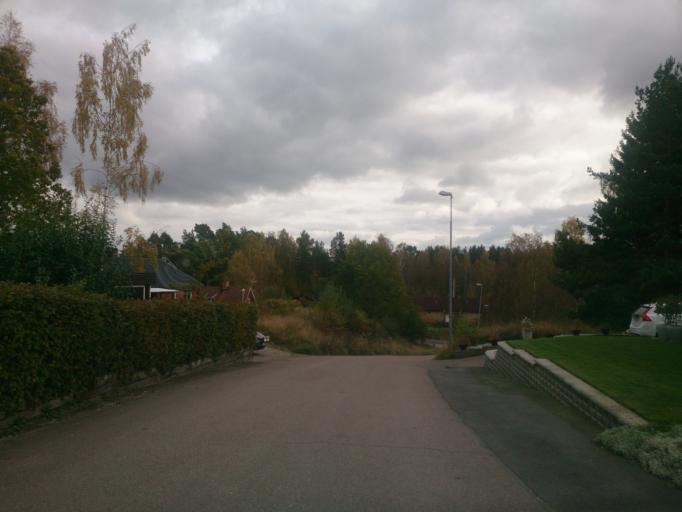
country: SE
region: OEstergoetland
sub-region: Atvidabergs Kommun
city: Atvidaberg
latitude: 58.2192
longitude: 16.0187
